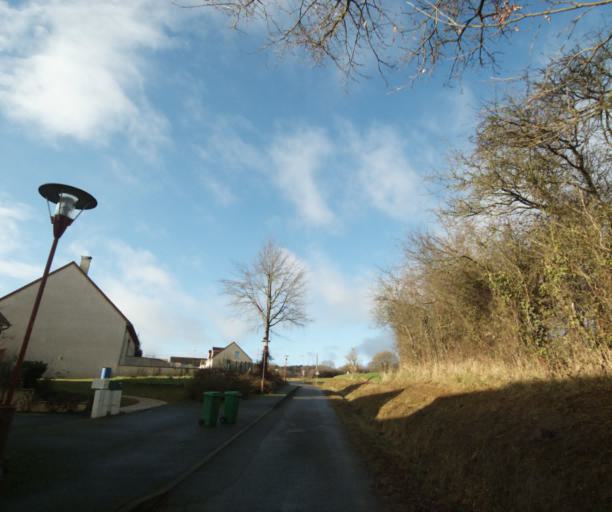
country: FR
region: Pays de la Loire
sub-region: Departement de la Sarthe
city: La Chapelle-Saint-Aubin
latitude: 48.0233
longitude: 0.1620
